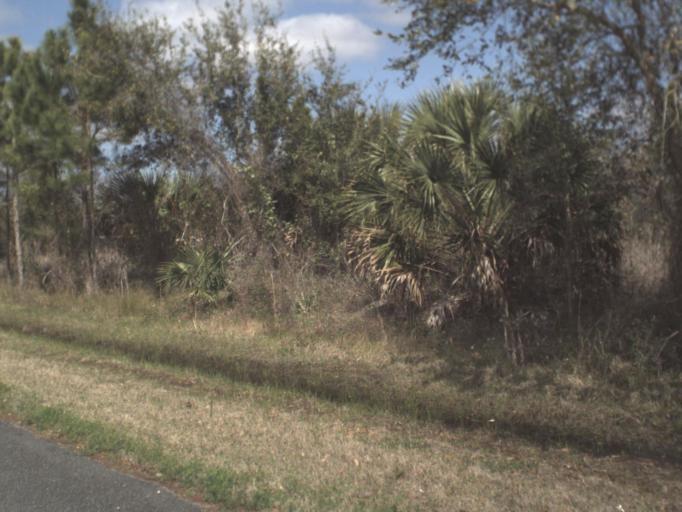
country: US
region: Florida
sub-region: Franklin County
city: Apalachicola
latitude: 29.7185
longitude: -85.0617
